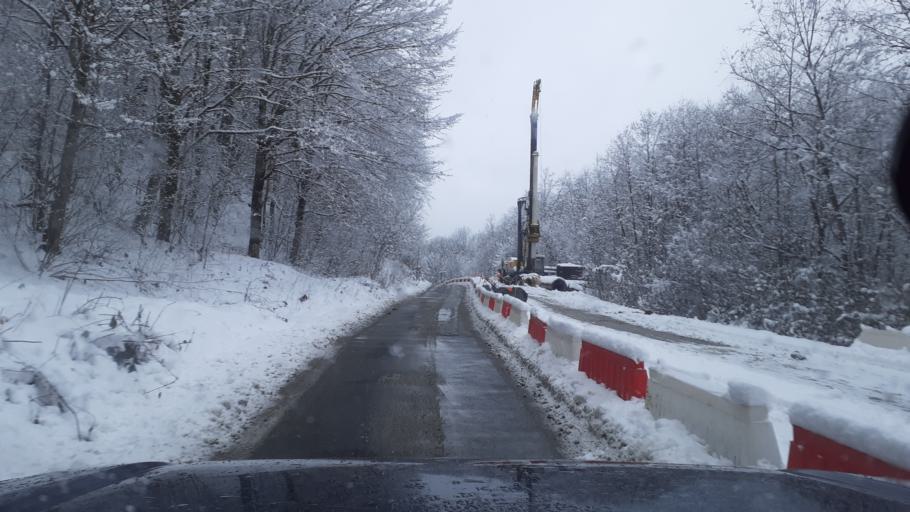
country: RU
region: Adygeya
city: Kamennomostskiy
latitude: 44.1931
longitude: 40.1715
